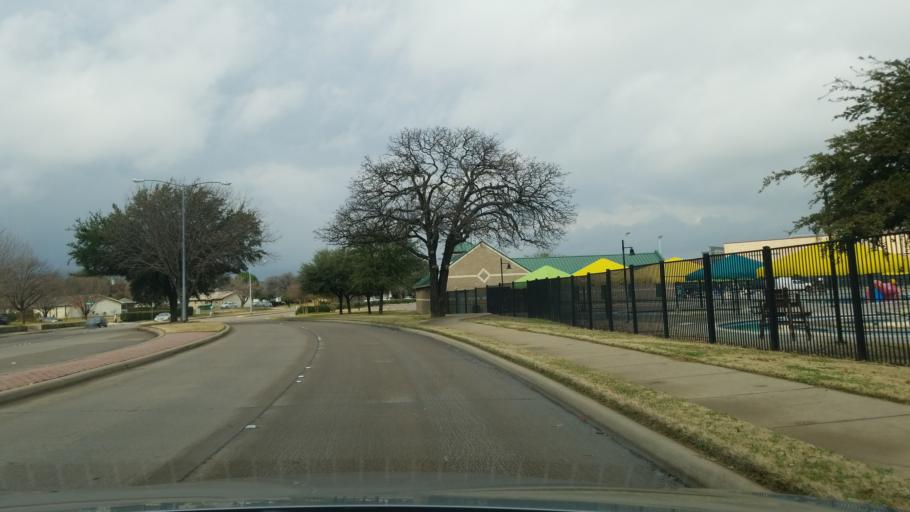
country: US
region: Texas
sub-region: Denton County
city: Lewisville
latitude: 33.0375
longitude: -97.0191
